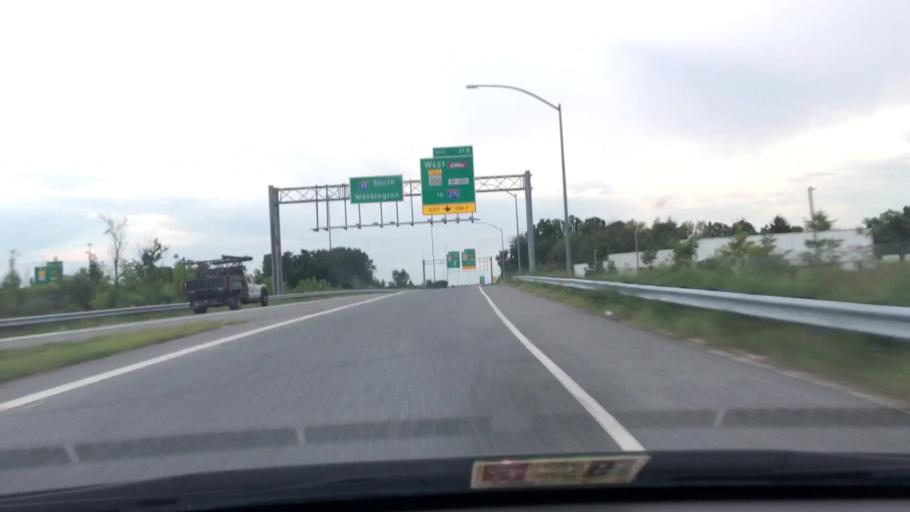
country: US
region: Maryland
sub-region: Prince George's County
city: West Laurel
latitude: 39.0821
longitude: -76.9012
